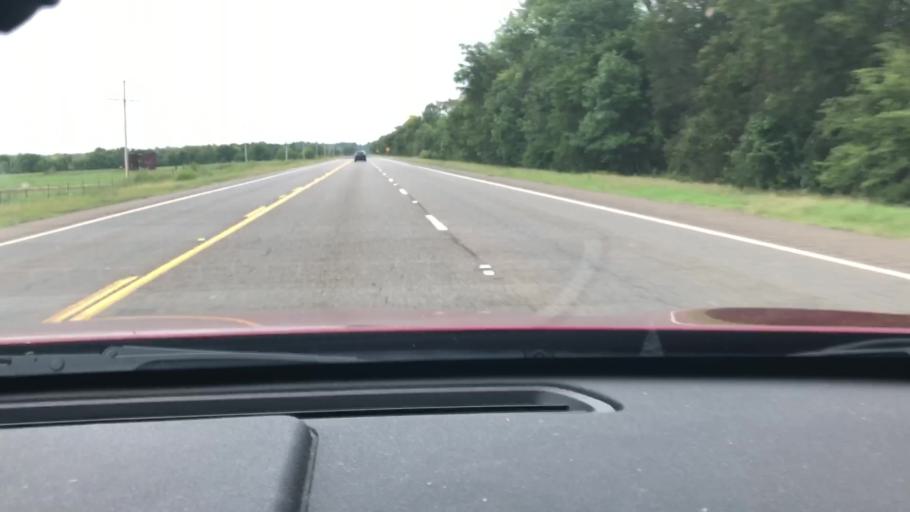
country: US
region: Arkansas
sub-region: Lafayette County
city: Lewisville
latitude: 33.3564
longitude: -93.6518
